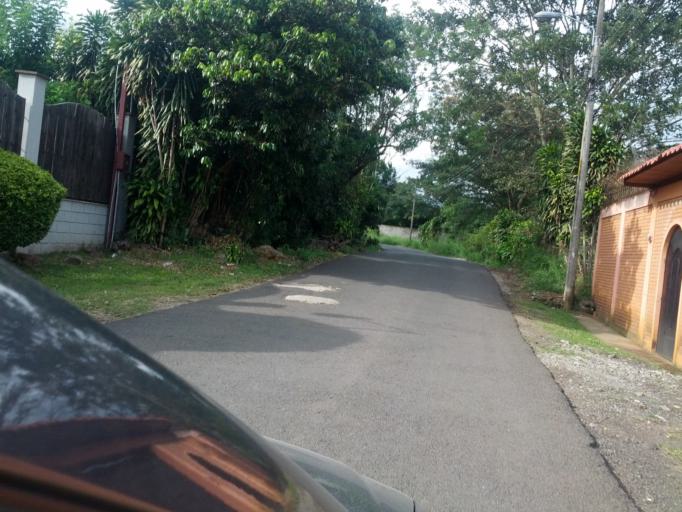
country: CR
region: Heredia
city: Llorente
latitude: 10.0190
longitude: -84.1749
